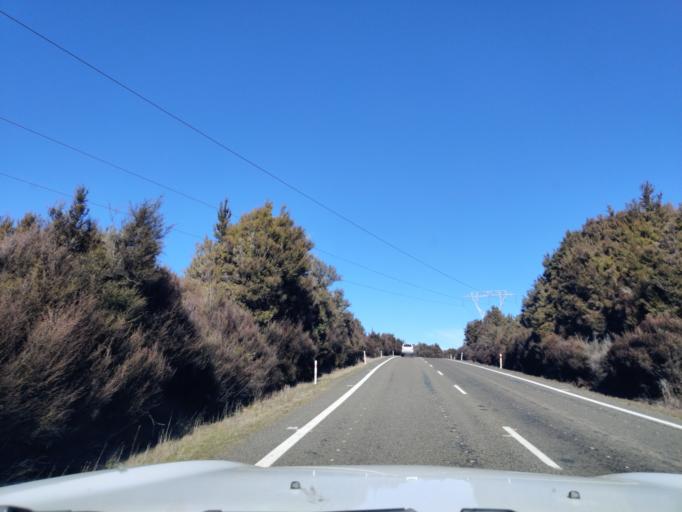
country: NZ
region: Waikato
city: Turangi
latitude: -39.2019
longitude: 175.7567
